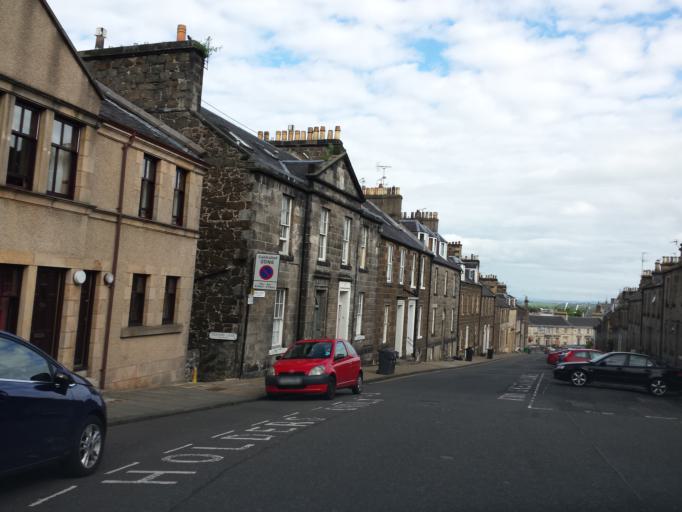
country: GB
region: Scotland
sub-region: Stirling
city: Stirling
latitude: 56.1233
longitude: -3.9413
